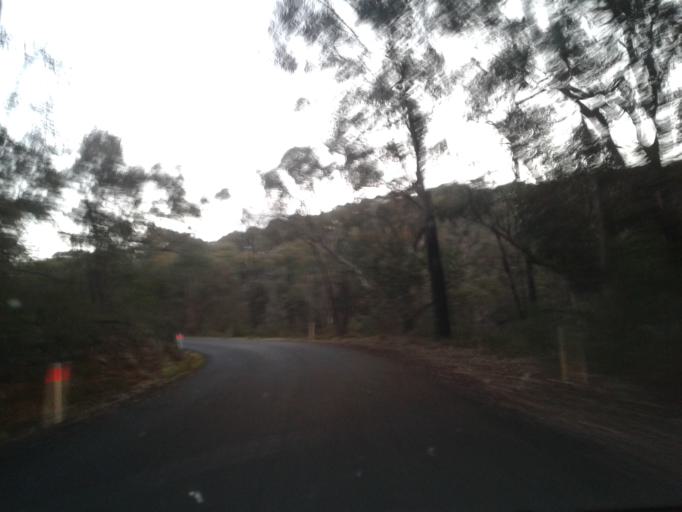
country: AU
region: Victoria
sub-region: Northern Grampians
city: Stawell
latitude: -37.1622
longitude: 142.4945
